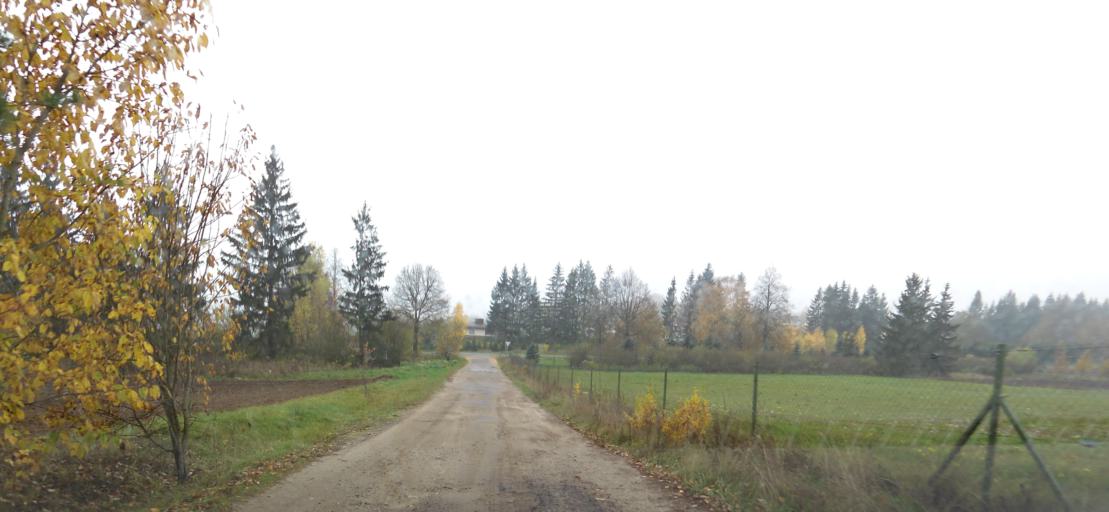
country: LT
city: Skaidiskes
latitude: 54.6184
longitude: 25.4694
